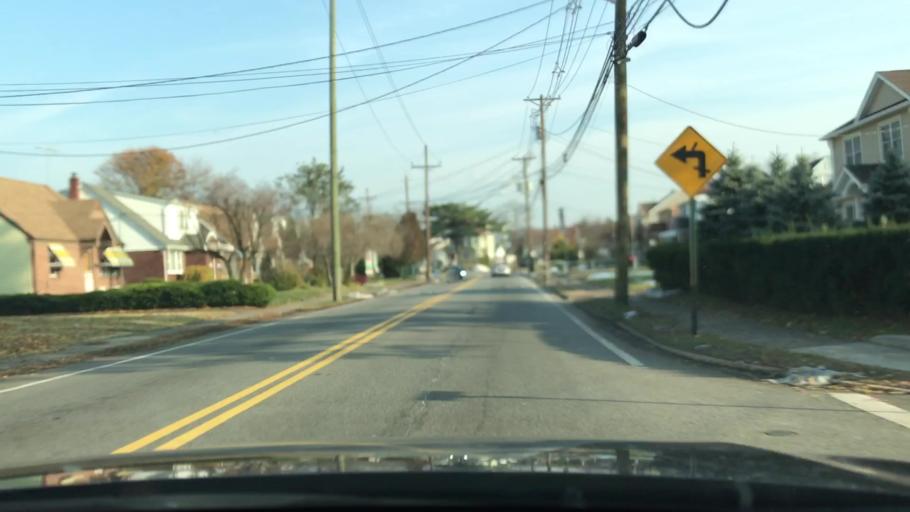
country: US
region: New Jersey
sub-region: Bergen County
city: Wallington
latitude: 40.8592
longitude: -74.1041
